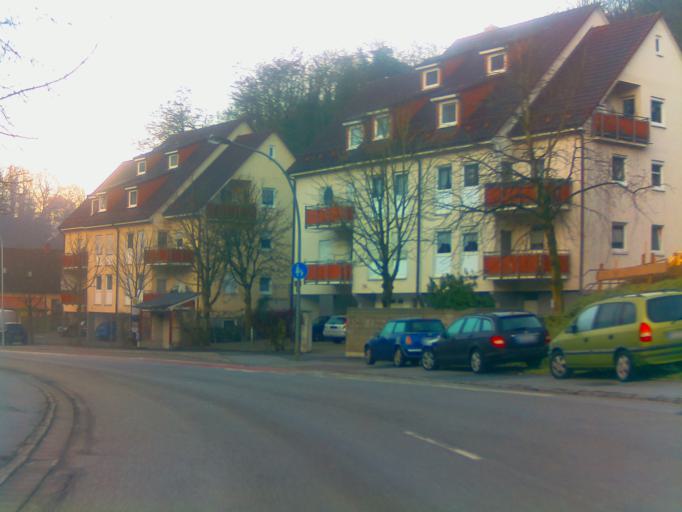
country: DE
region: Hesse
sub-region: Regierungsbezirk Darmstadt
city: Heppenheim an der Bergstrasse
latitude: 49.6457
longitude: 8.6593
